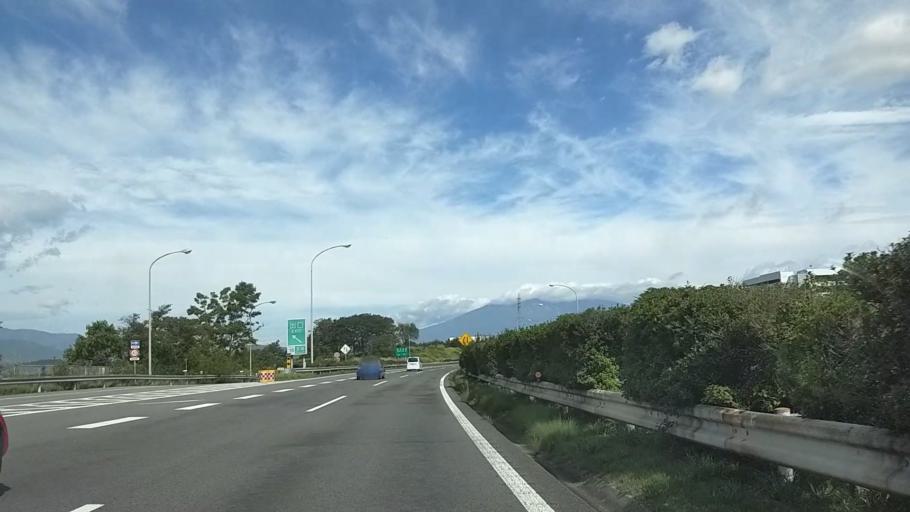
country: JP
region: Yamanashi
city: Nirasaki
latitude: 35.7173
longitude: 138.4666
